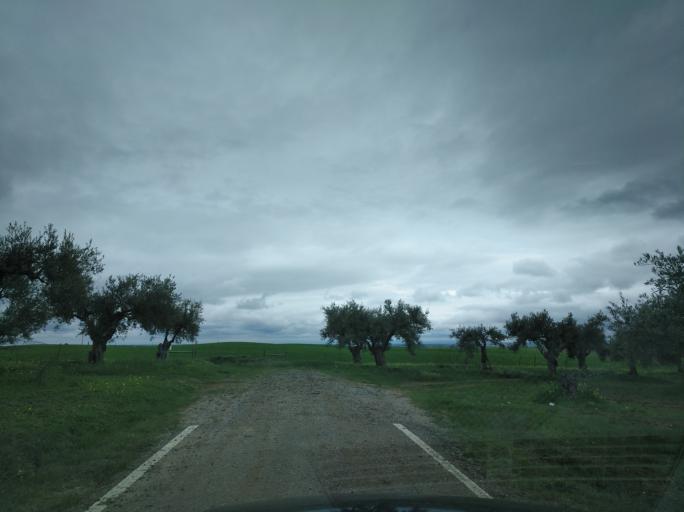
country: PT
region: Portalegre
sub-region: Campo Maior
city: Campo Maior
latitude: 38.9762
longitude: -7.0280
